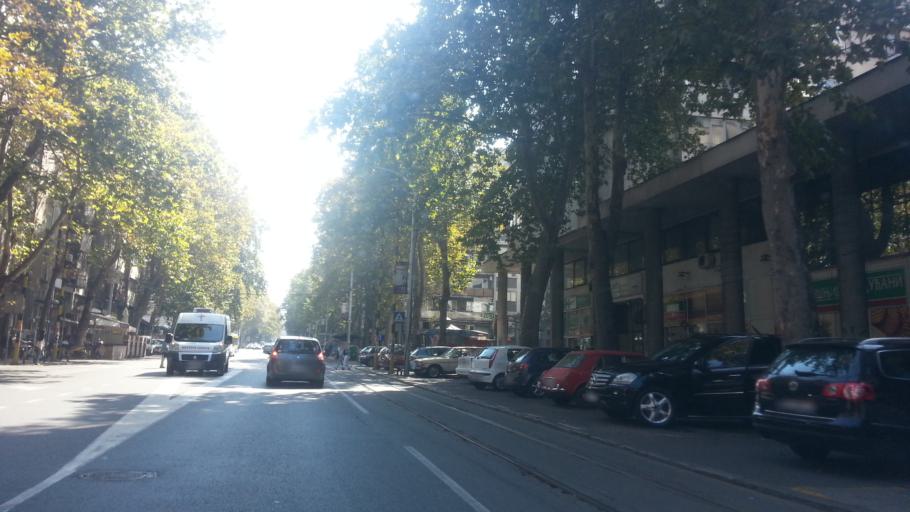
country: RS
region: Central Serbia
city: Belgrade
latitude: 44.8113
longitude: 20.4738
